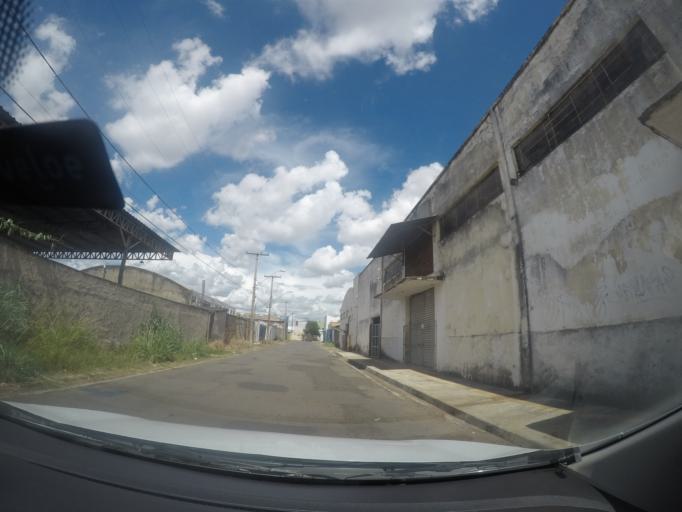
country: BR
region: Goias
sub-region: Goiania
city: Goiania
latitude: -16.6686
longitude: -49.3082
